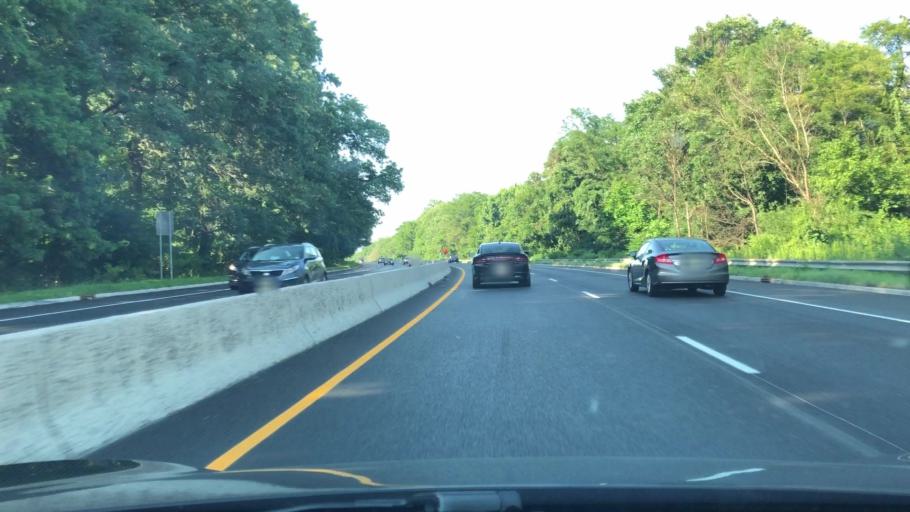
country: US
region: New Jersey
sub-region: Mercer County
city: Mercerville
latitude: 40.2538
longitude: -74.7202
